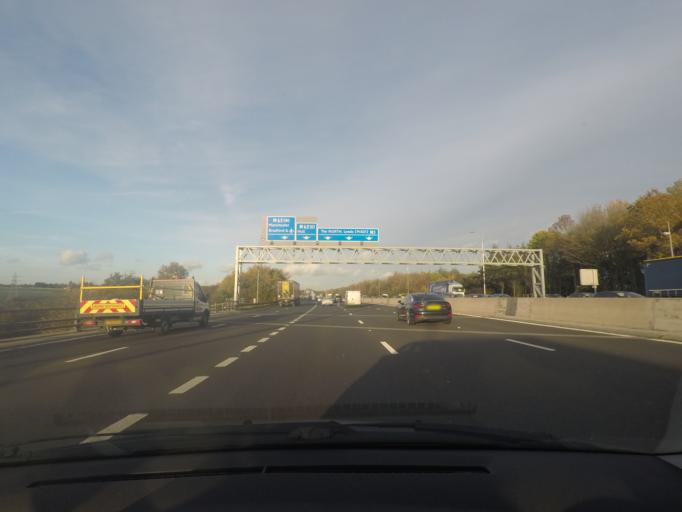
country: GB
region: England
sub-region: City and Borough of Leeds
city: Lofthouse
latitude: 53.7245
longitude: -1.5183
